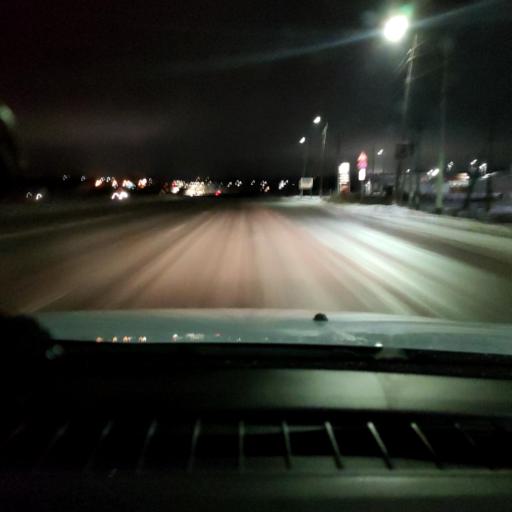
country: RU
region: Samara
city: Smyshlyayevka
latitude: 53.2617
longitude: 50.5015
